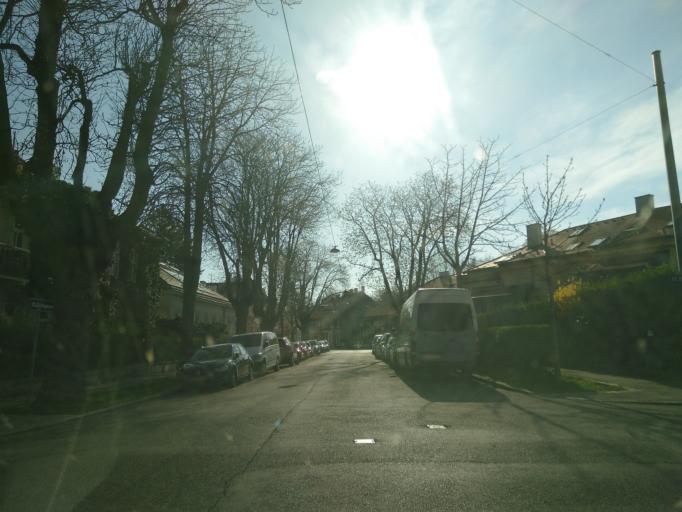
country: AT
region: Lower Austria
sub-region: Politischer Bezirk Modling
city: Perchtoldsdorf
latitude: 48.1832
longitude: 16.2884
